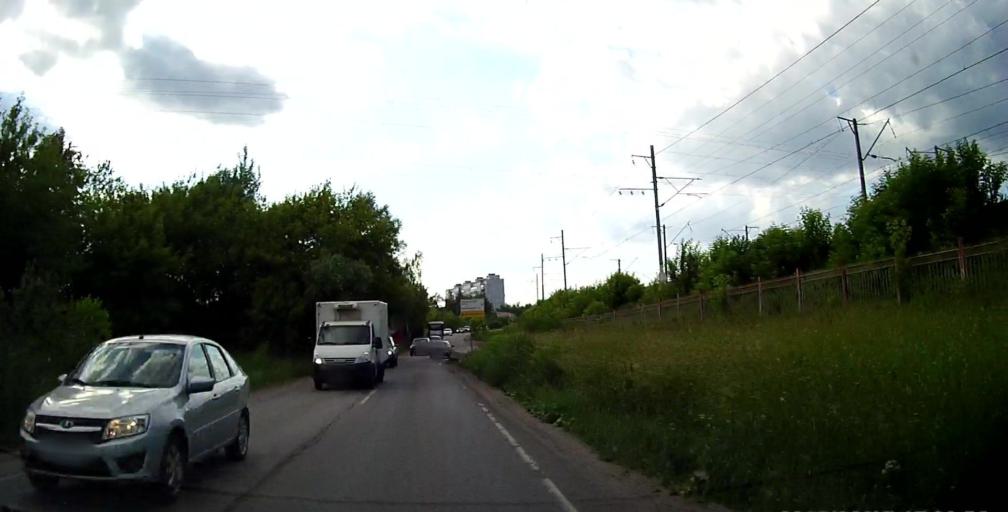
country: RU
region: Moskovskaya
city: Shcherbinka
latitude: 55.5136
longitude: 37.5418
